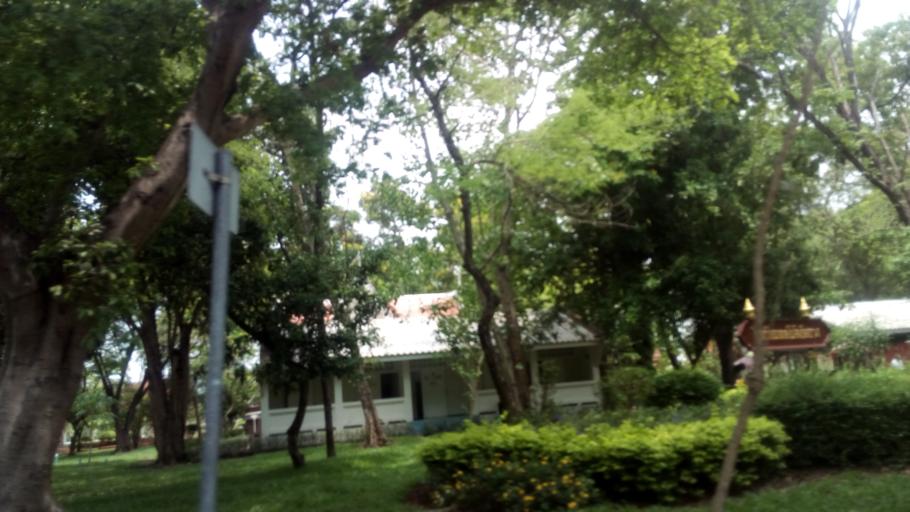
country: TH
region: Bangkok
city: Thawi Watthana
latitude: 13.7753
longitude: 100.3198
